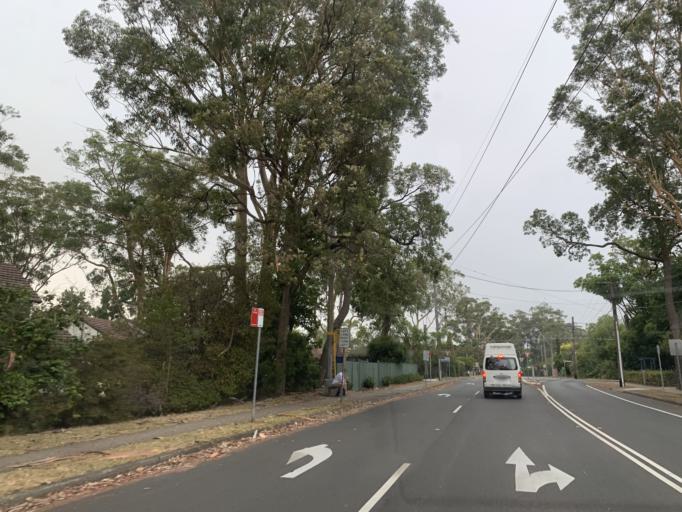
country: AU
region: New South Wales
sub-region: The Hills Shire
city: West Pennant
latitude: -33.7392
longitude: 151.0477
